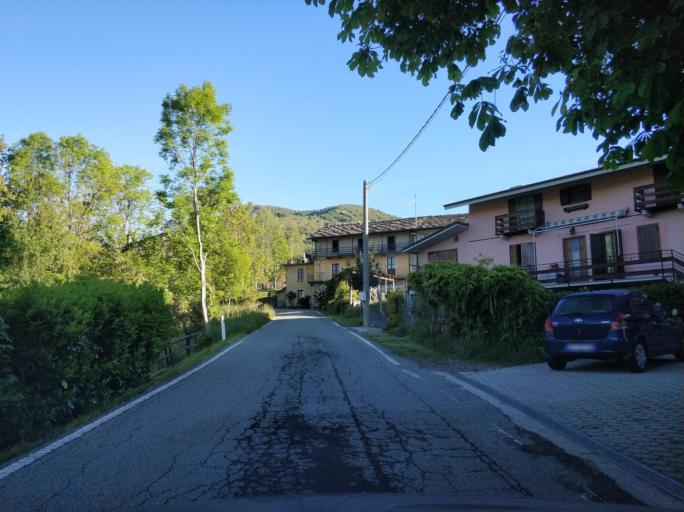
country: IT
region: Piedmont
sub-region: Provincia di Torino
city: Coassolo
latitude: 45.2989
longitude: 7.4667
